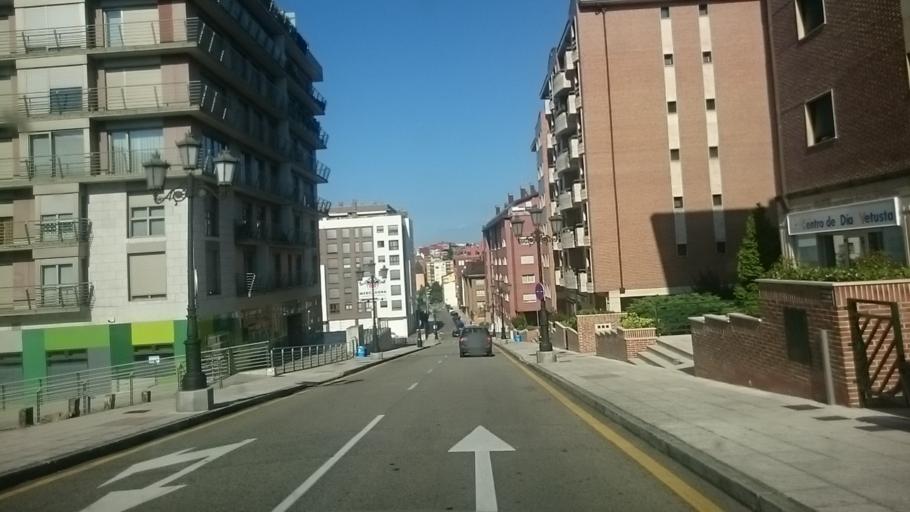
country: ES
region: Asturias
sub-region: Province of Asturias
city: Oviedo
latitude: 43.3538
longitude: -5.8609
